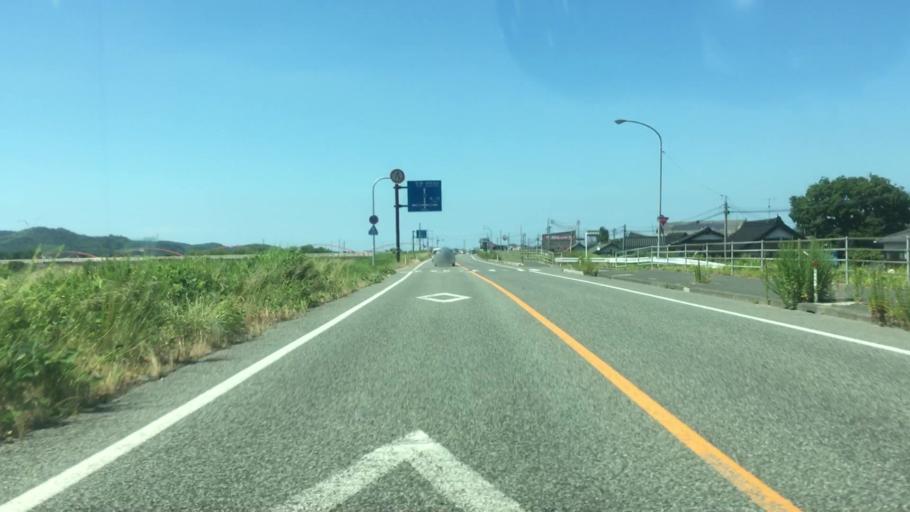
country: JP
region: Tottori
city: Tottori
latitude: 35.4616
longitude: 134.2150
